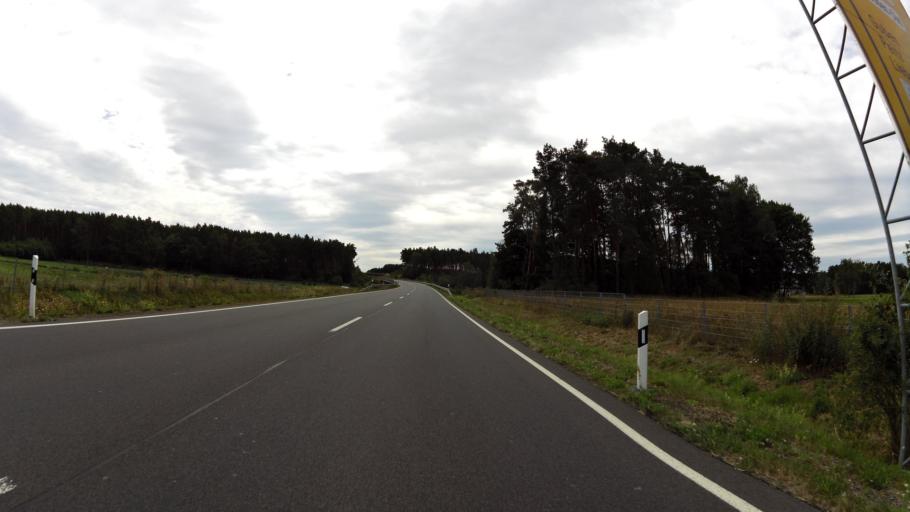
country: DE
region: Brandenburg
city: Schenkendobern
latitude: 51.9593
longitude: 14.6473
